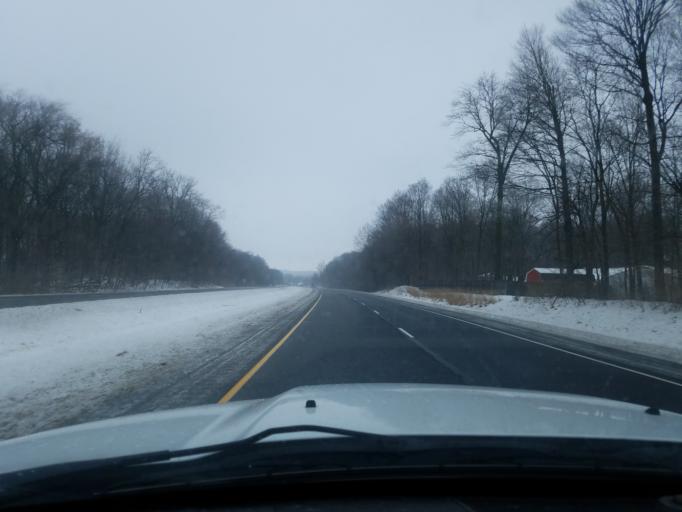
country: US
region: Indiana
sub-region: Miami County
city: Peru
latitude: 40.7397
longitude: -86.1256
